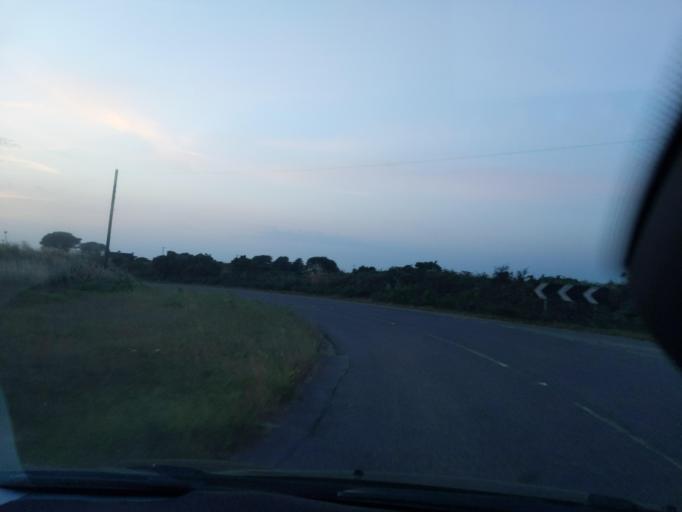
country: GB
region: England
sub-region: Cornwall
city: Camborne
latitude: 50.1826
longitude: -5.3115
